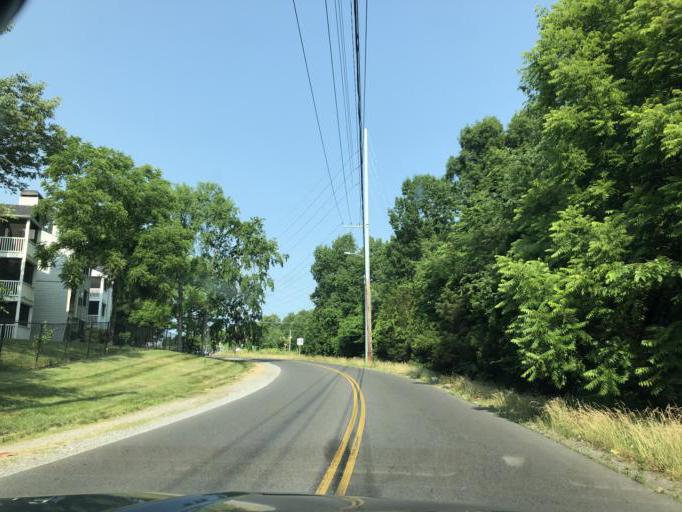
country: US
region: Tennessee
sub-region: Rutherford County
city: La Vergne
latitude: 36.0554
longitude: -86.6398
